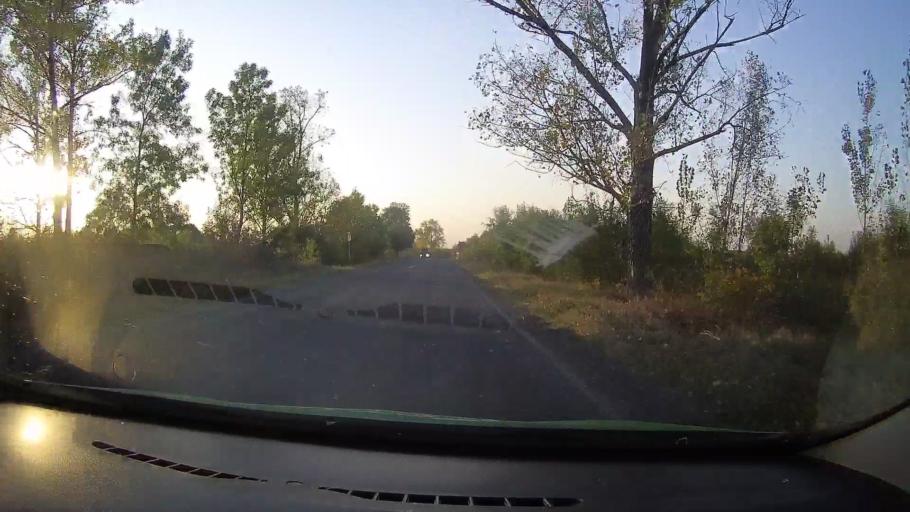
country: RO
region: Arad
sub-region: Comuna Bocsig
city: Bocsig
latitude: 46.4242
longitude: 21.9163
